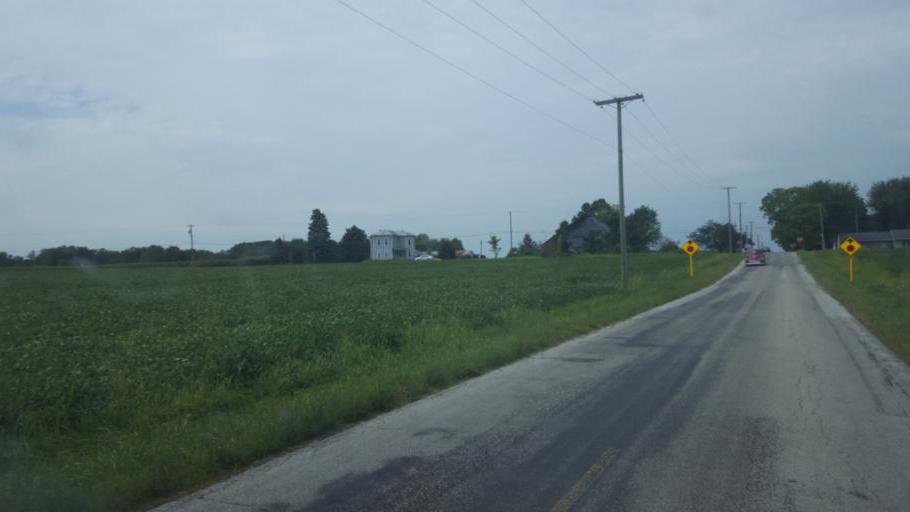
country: US
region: Ohio
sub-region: Marion County
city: Marion
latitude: 40.5204
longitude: -83.0986
